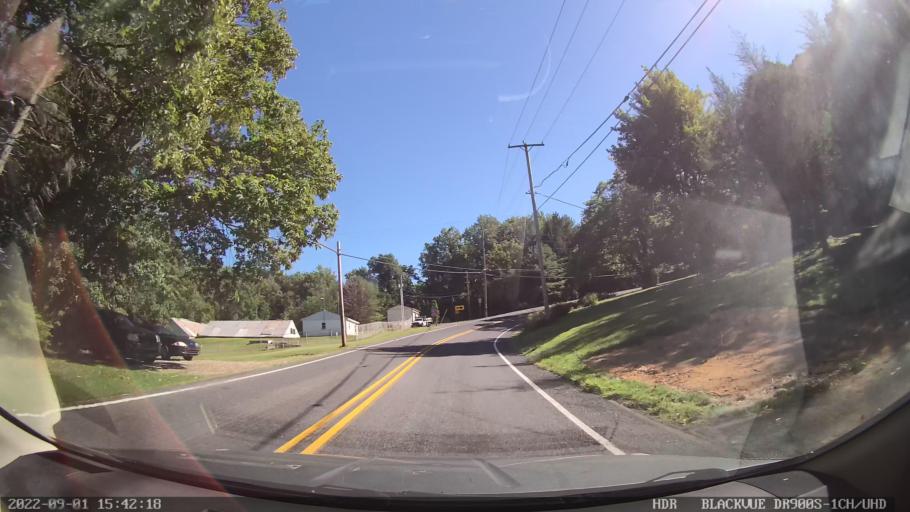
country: US
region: Pennsylvania
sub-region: Berks County
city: Topton
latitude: 40.4907
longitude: -75.6999
